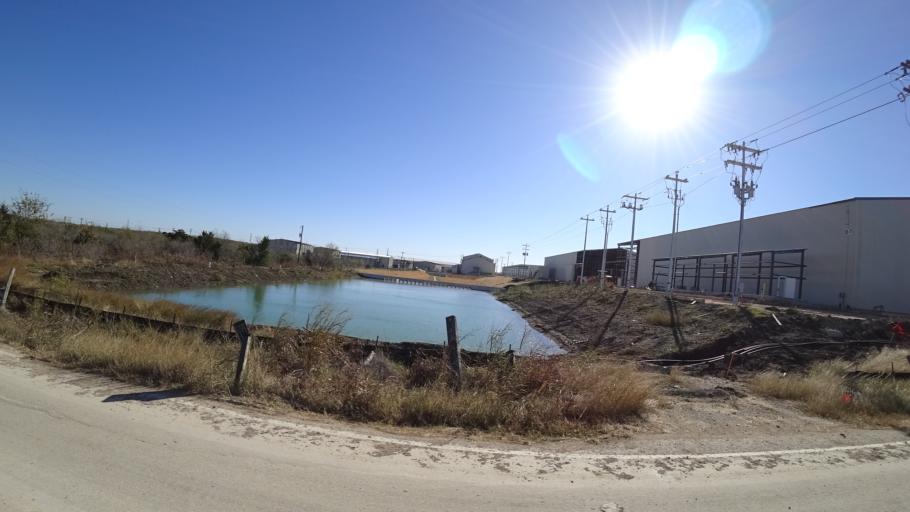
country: US
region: Texas
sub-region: Travis County
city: Onion Creek
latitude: 30.1202
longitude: -97.6687
